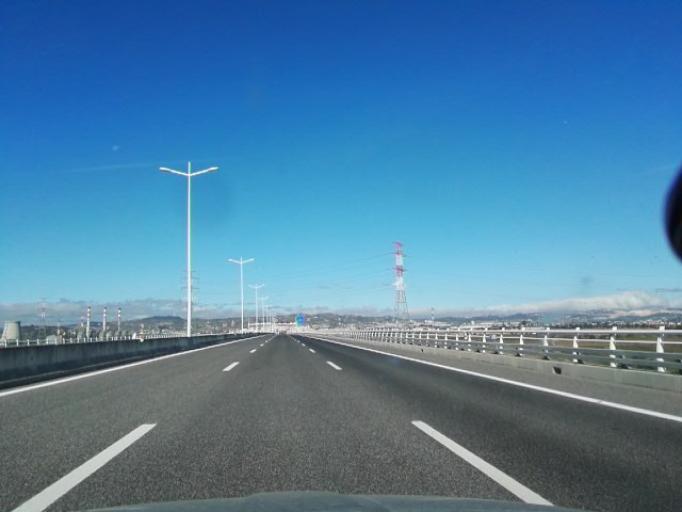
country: PT
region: Lisbon
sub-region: Alenquer
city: Carregado
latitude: 39.0132
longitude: -8.9359
